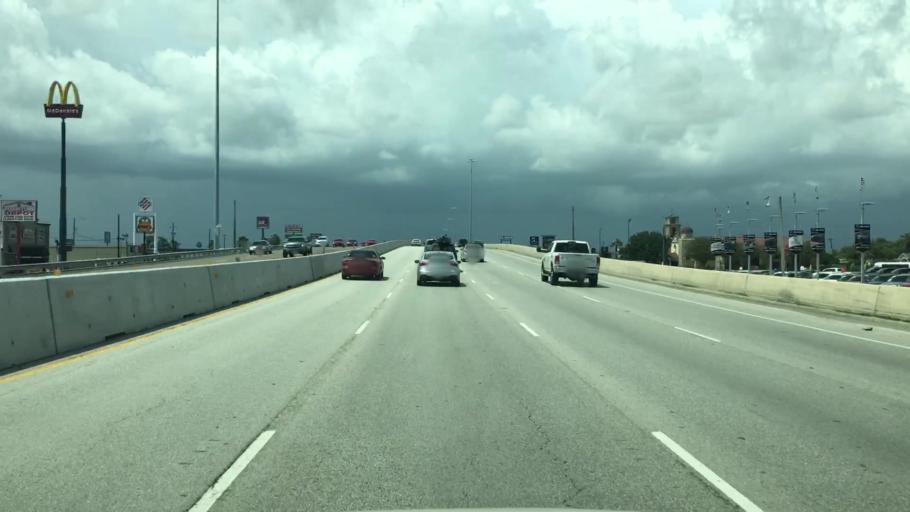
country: US
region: Texas
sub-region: Nueces County
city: Corpus Christi
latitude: 27.7275
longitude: -97.4104
